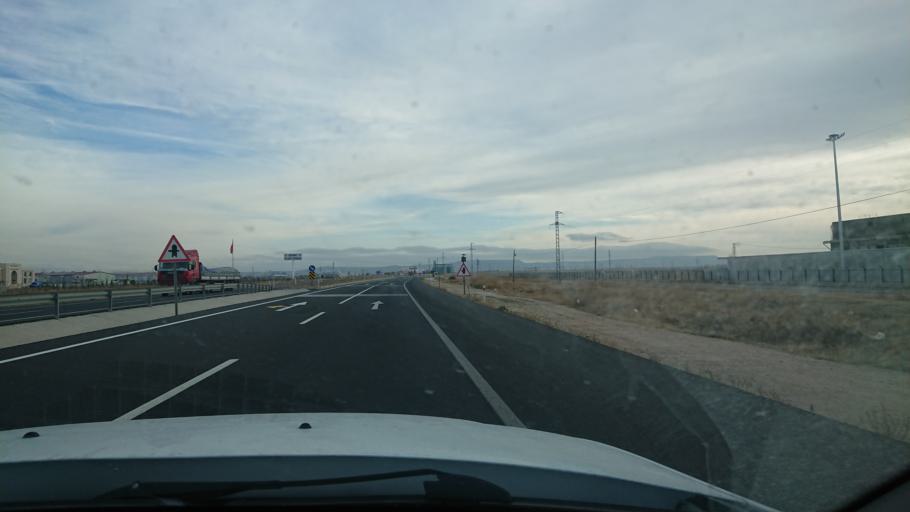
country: TR
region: Aksaray
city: Aksaray
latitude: 38.3356
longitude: 33.9301
